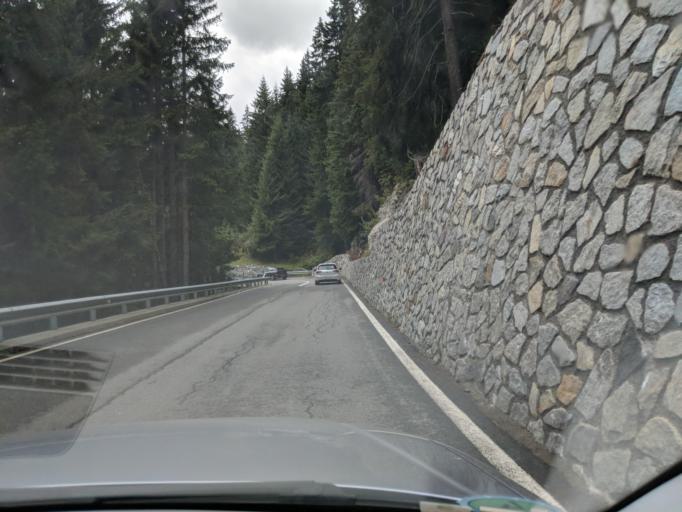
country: IT
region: Trentino-Alto Adige
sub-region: Bolzano
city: Racines
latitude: 46.8290
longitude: 11.3032
